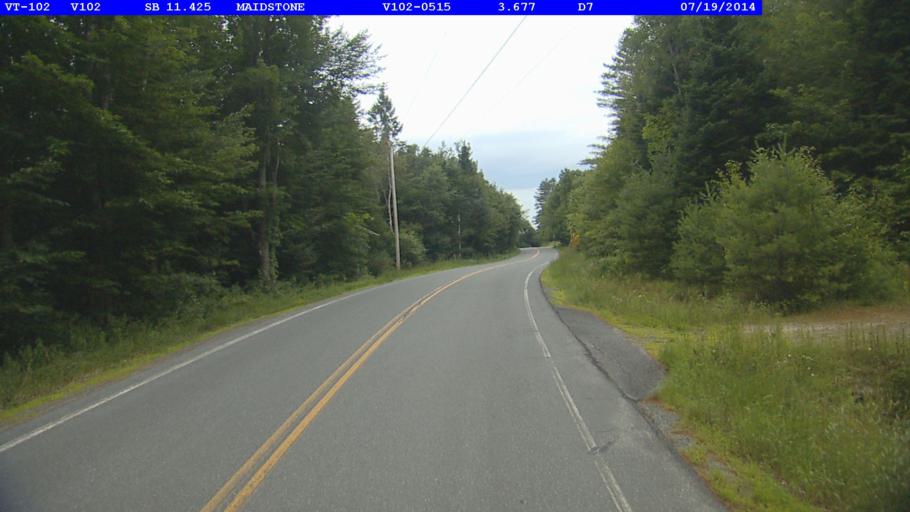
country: US
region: New Hampshire
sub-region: Coos County
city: Stratford
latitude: 44.6139
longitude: -71.5596
